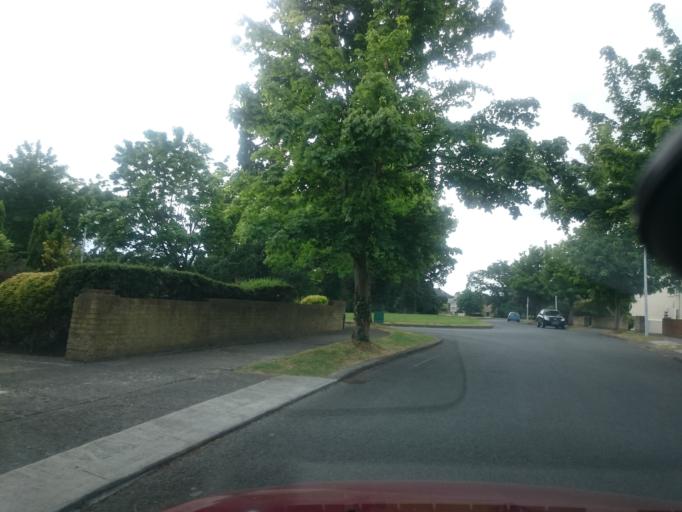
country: IE
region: Leinster
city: Mount Merrion
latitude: 53.3017
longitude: -6.2231
